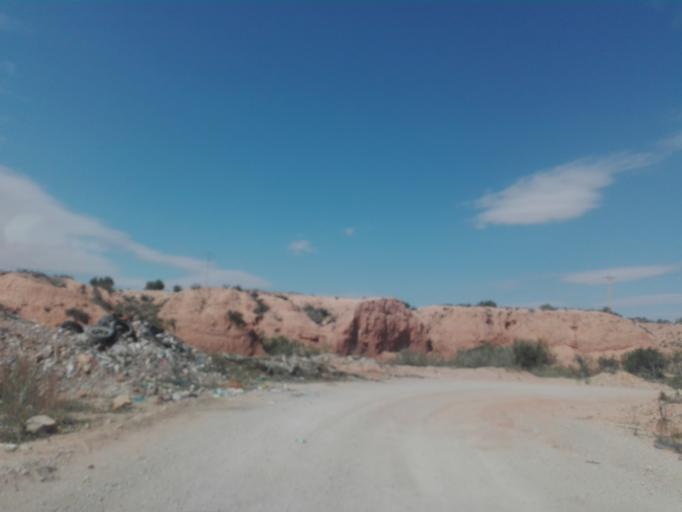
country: TN
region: Safaqis
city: Sfax
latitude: 34.6861
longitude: 10.5601
